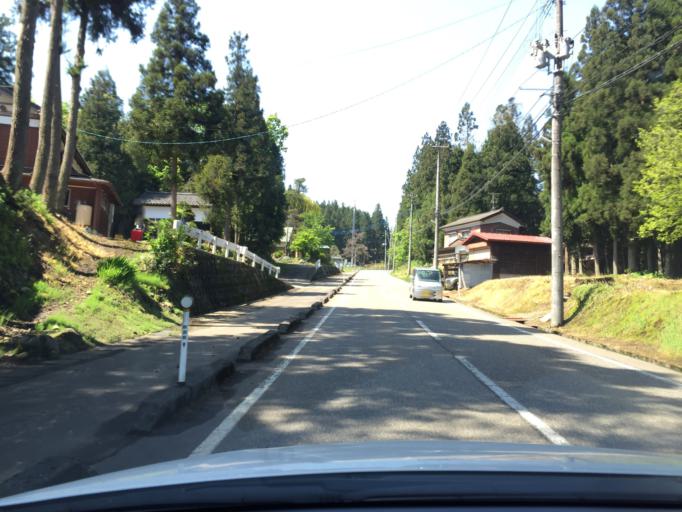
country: JP
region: Niigata
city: Kamo
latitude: 37.5792
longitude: 139.0721
